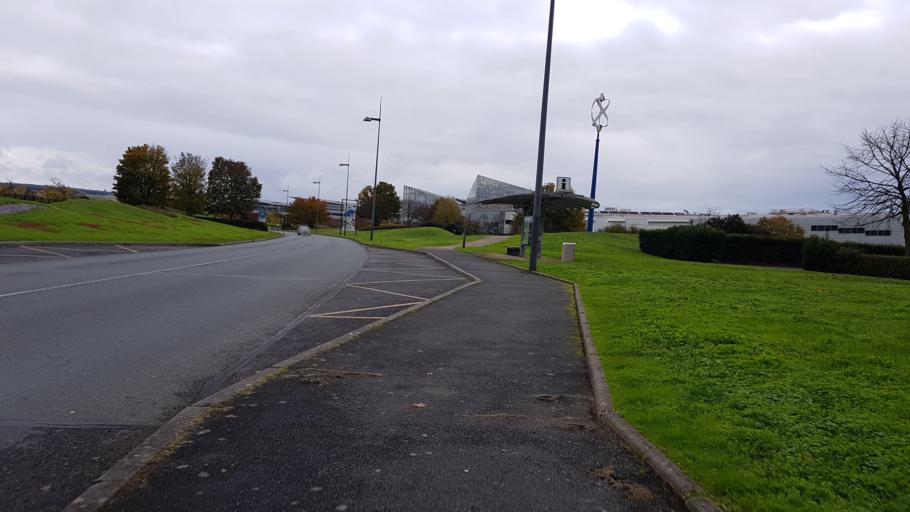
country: FR
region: Poitou-Charentes
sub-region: Departement de la Vienne
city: Chasseneuil-du-Poitou
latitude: 46.6627
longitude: 0.3618
